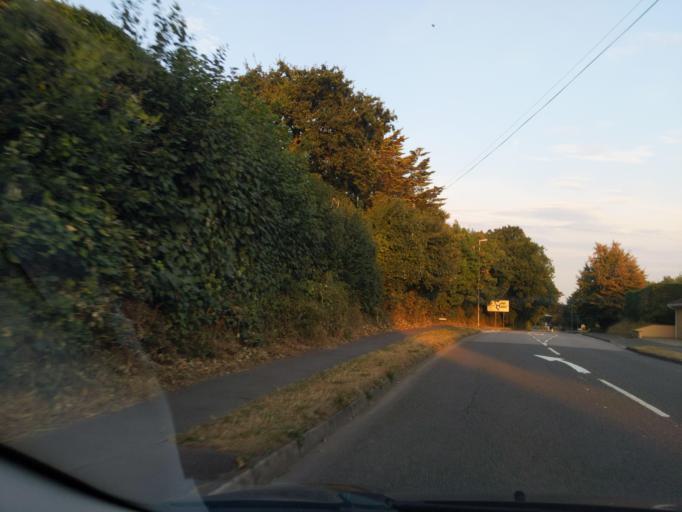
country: GB
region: England
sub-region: Cornwall
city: Liskeard
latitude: 50.4519
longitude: -4.4566
